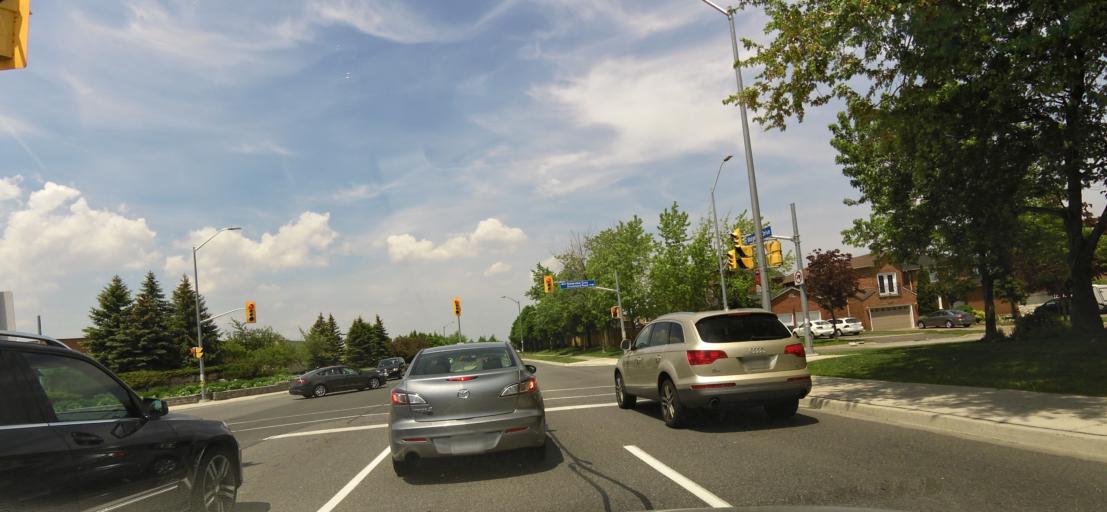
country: CA
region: Ontario
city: Mississauga
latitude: 43.5272
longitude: -79.7133
